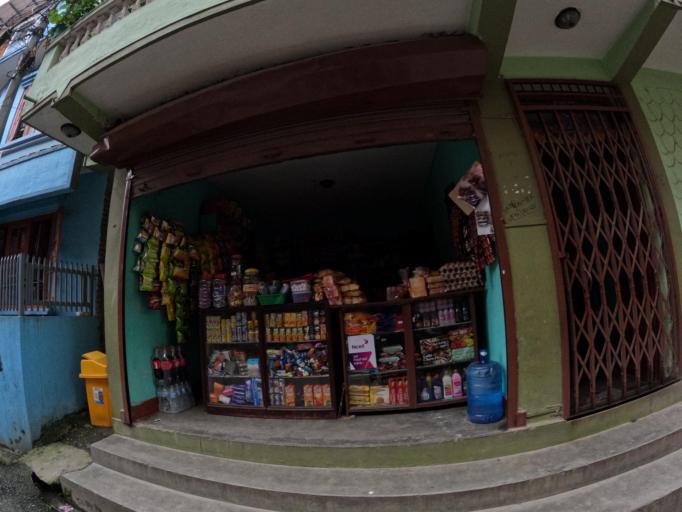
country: NP
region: Central Region
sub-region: Bagmati Zone
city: Kathmandu
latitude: 27.7415
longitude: 85.3165
